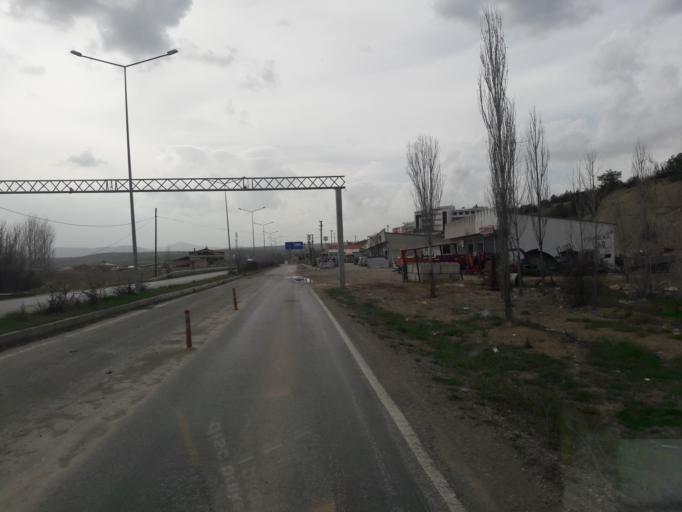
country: TR
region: Gumushane
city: Siran
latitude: 40.1775
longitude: 39.1278
